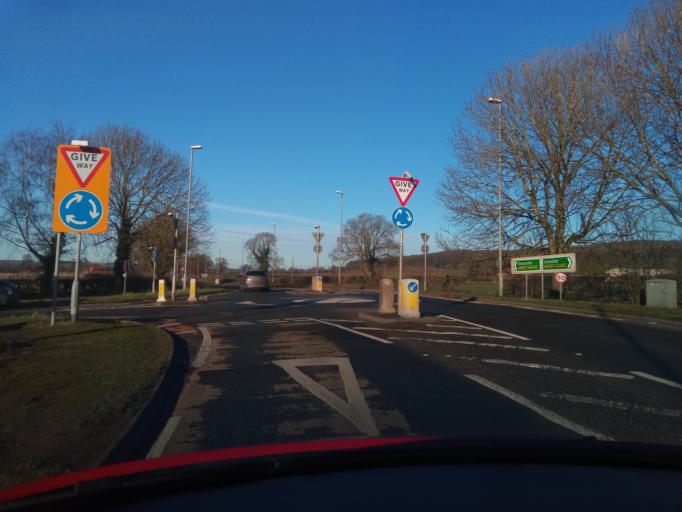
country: GB
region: England
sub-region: Nottinghamshire
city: Lowdham
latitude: 53.0325
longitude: -1.0418
